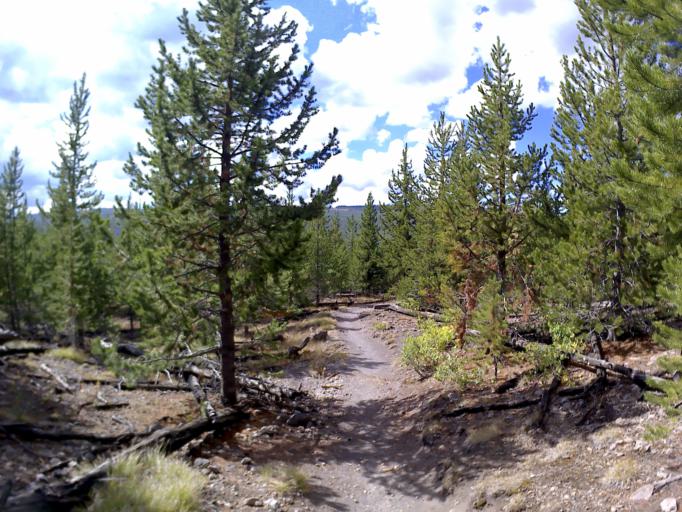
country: US
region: Montana
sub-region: Gallatin County
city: West Yellowstone
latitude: 44.4866
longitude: -110.8711
